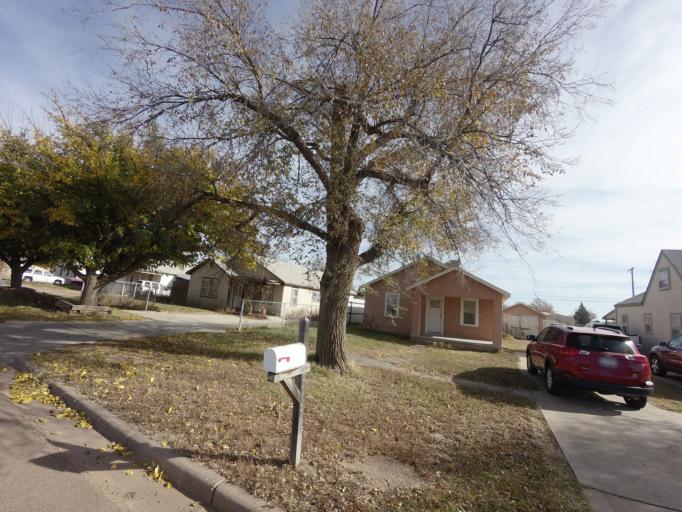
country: US
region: New Mexico
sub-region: Curry County
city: Clovis
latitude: 34.4051
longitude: -103.1952
